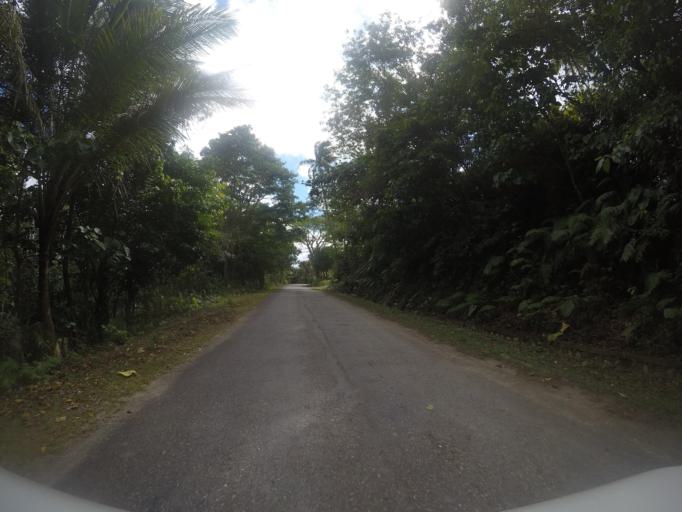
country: TL
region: Lautem
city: Lospalos
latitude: -8.5336
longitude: 126.9301
